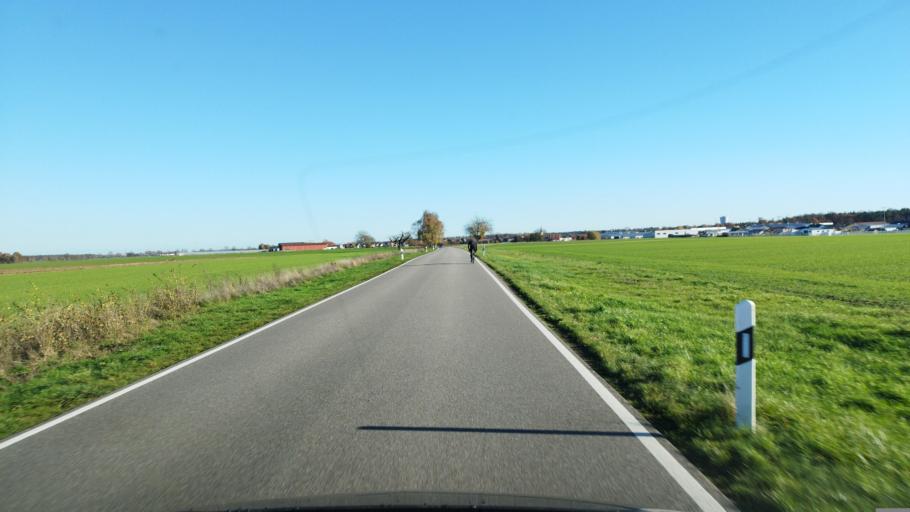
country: DE
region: Rheinland-Pfalz
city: Hatzenbuhl
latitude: 49.1162
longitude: 8.2234
